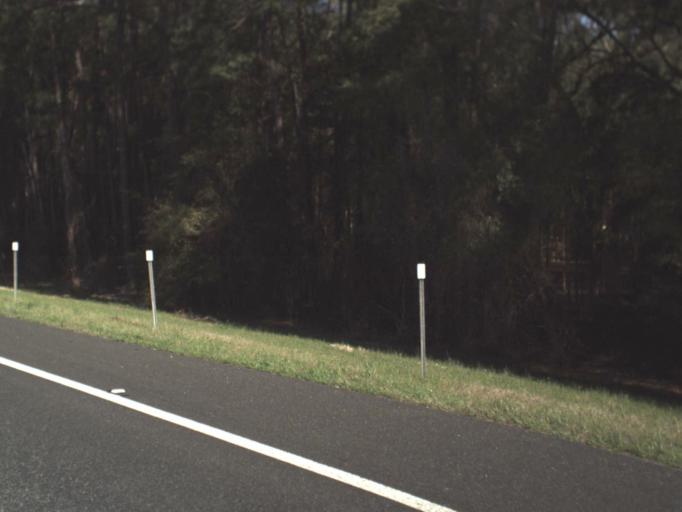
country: US
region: Florida
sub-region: Leon County
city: Tallahassee
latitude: 30.4897
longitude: -84.1650
